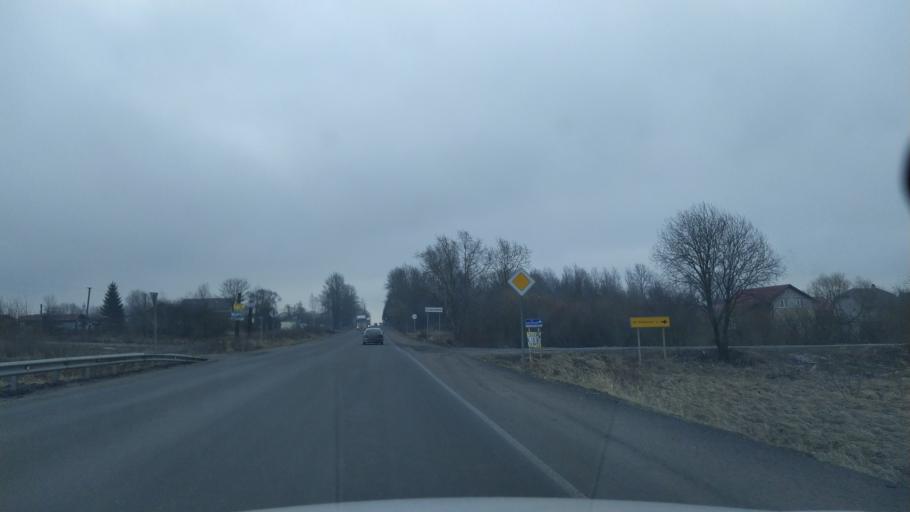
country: RU
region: St.-Petersburg
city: Aleksandrovskaya
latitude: 59.7257
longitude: 30.2484
